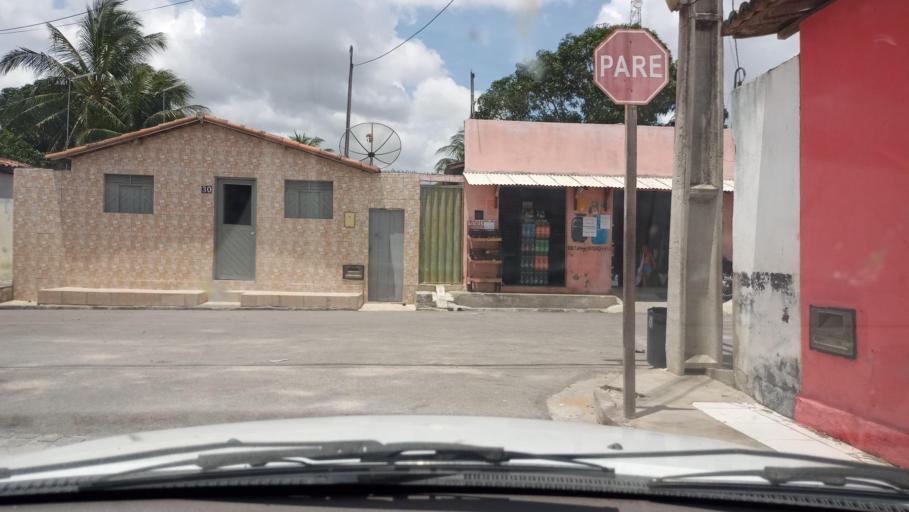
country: BR
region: Rio Grande do Norte
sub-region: Tangara
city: Tangara
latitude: -6.0970
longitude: -35.7095
